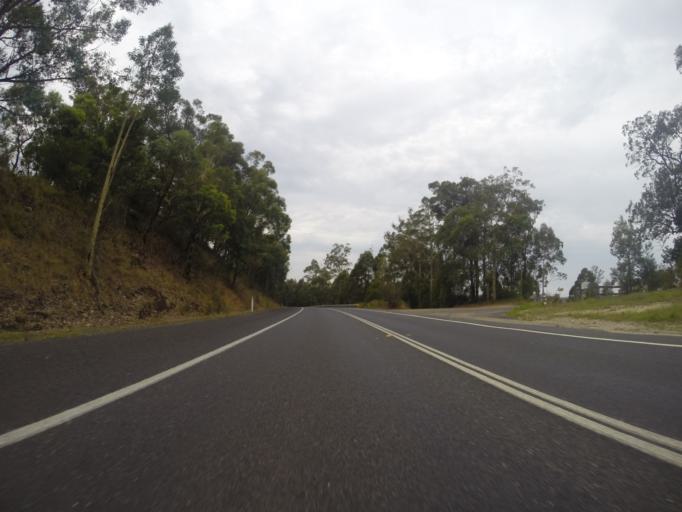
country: AU
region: New South Wales
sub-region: Eurobodalla
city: Batemans Bay
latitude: -35.6811
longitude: 150.2049
